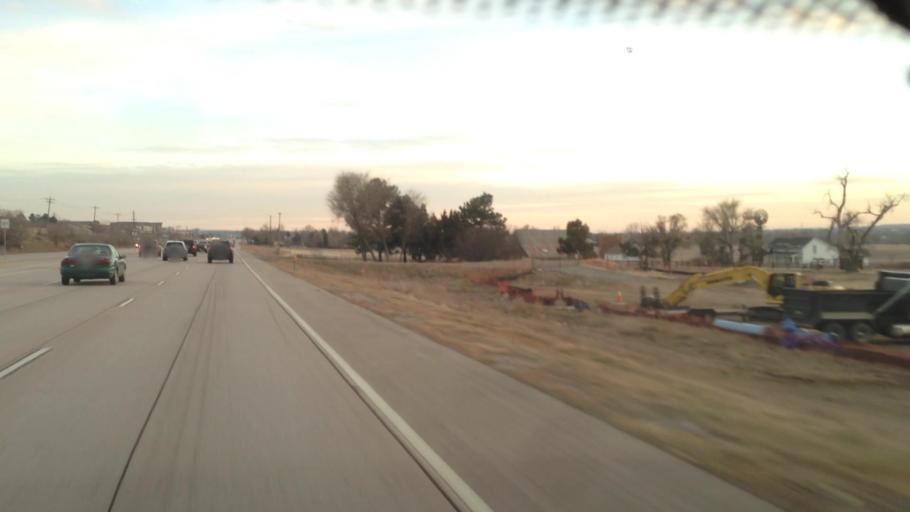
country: US
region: Colorado
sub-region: Douglas County
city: Stonegate
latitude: 39.5698
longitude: -104.7878
